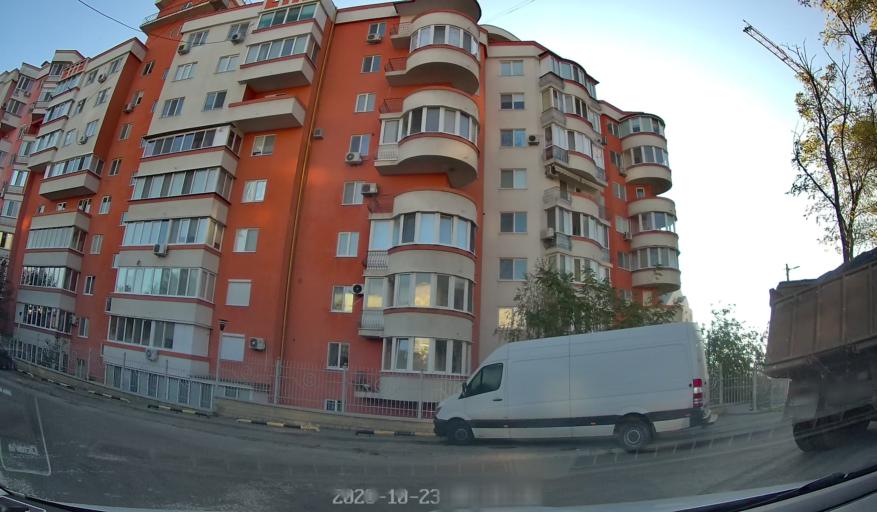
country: MD
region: Chisinau
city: Chisinau
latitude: 46.9979
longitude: 28.8371
